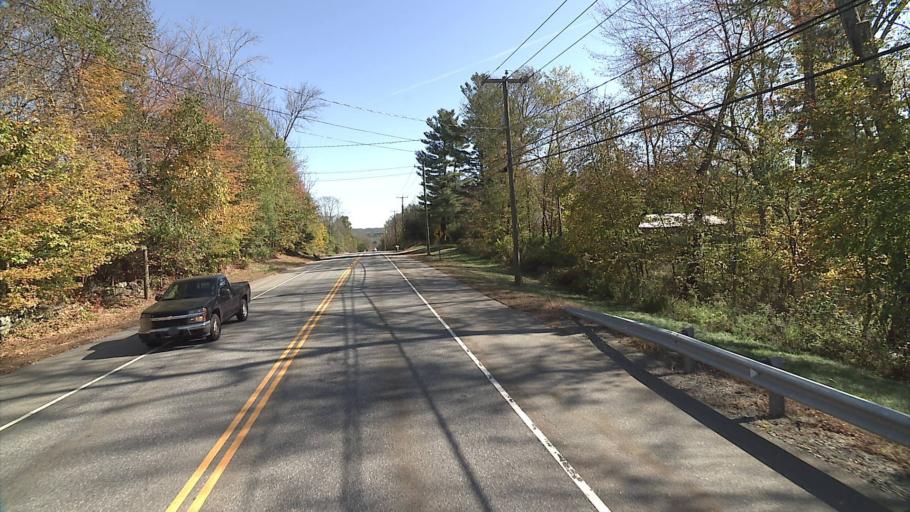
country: US
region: Connecticut
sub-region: Windham County
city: Wauregan
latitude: 41.7827
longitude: -71.9758
